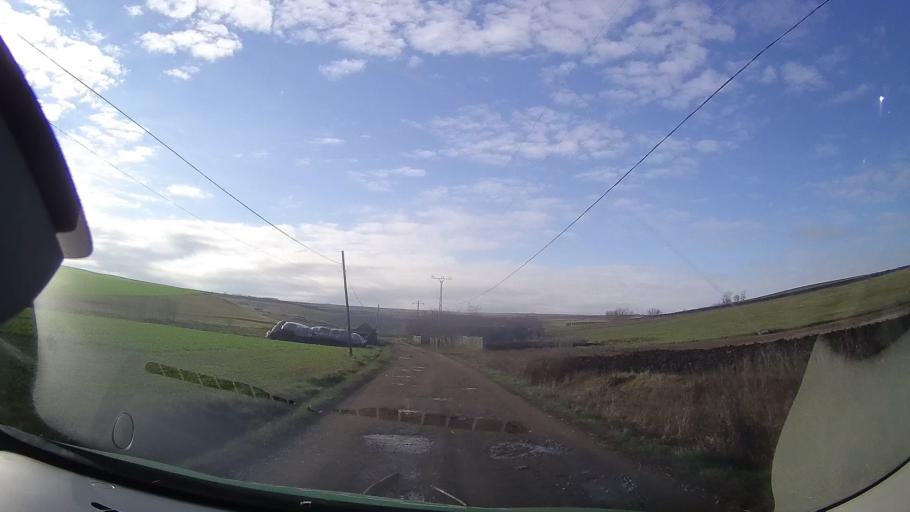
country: RO
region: Mures
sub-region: Comuna Saulia
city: Saulia
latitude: 46.6128
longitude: 24.2372
